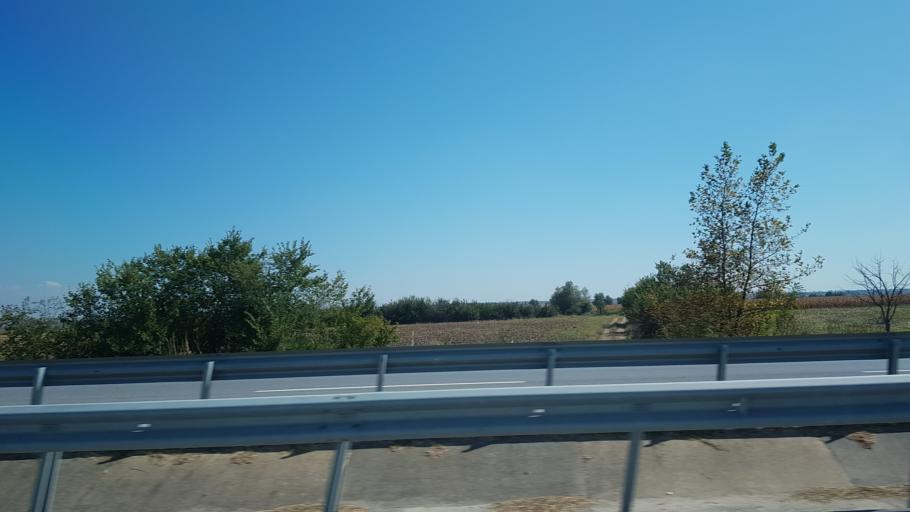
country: TR
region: Kirklareli
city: Inece
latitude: 41.5725
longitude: 27.1478
